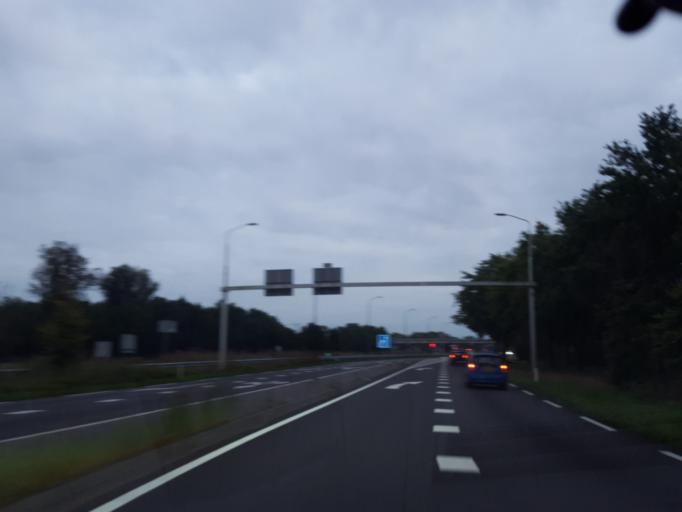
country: NL
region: North Brabant
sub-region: Gemeente Someren
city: Someren
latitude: 51.4206
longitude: 5.6991
